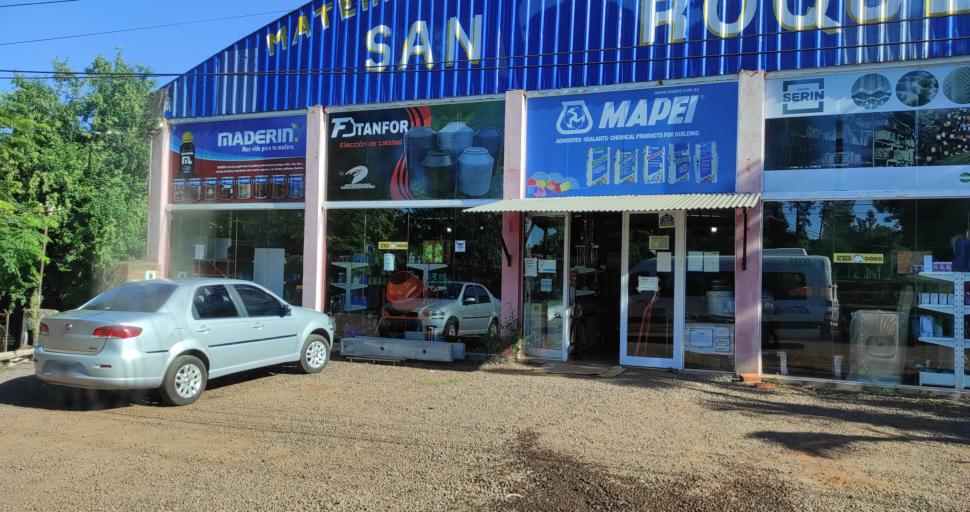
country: AR
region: Misiones
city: El Soberbio
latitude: -27.2942
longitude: -54.1972
